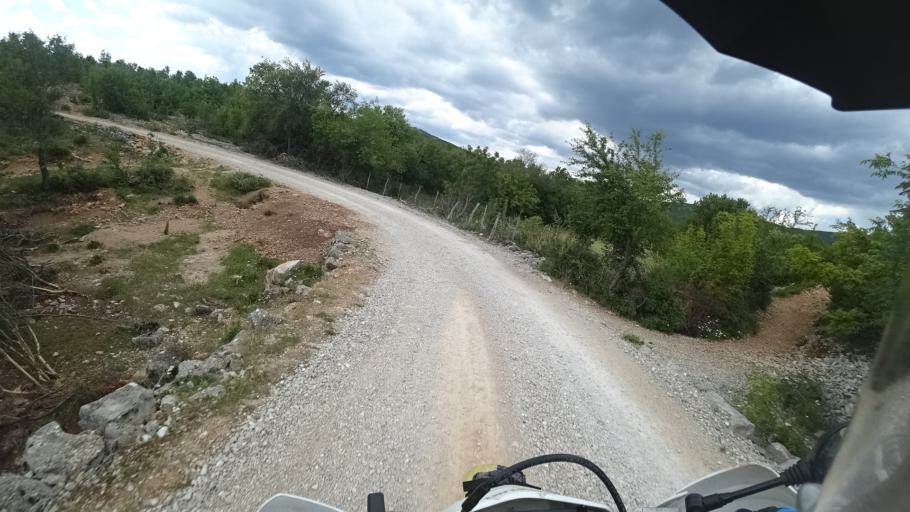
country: HR
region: Sibensko-Kniniska
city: Kistanje
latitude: 44.0962
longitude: 16.0092
